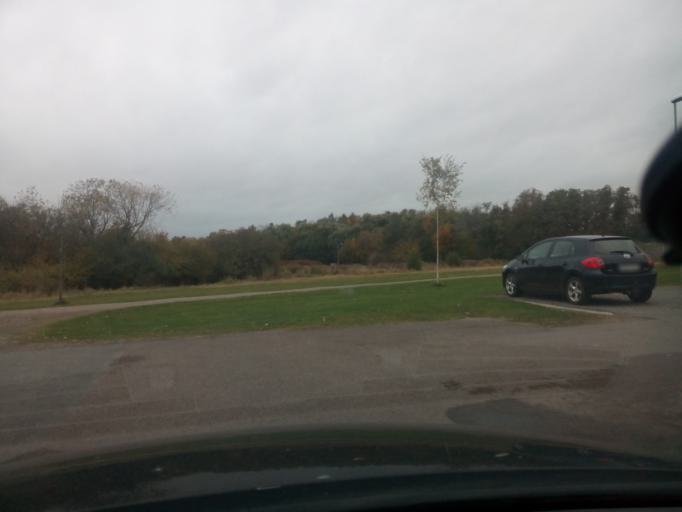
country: SE
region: Soedermanland
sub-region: Nykopings Kommun
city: Nykoping
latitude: 58.7465
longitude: 17.0364
